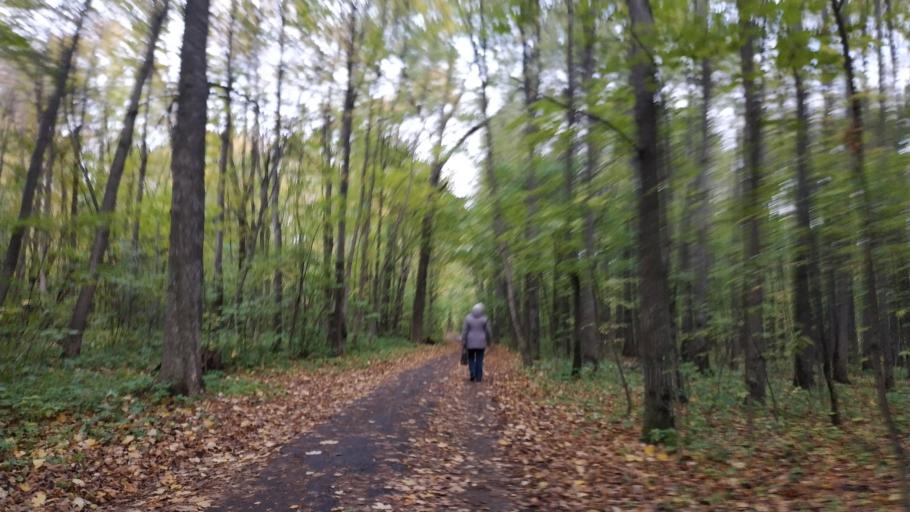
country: RU
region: Chuvashia
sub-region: Cheboksarskiy Rayon
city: Cheboksary
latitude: 56.1359
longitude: 47.1741
